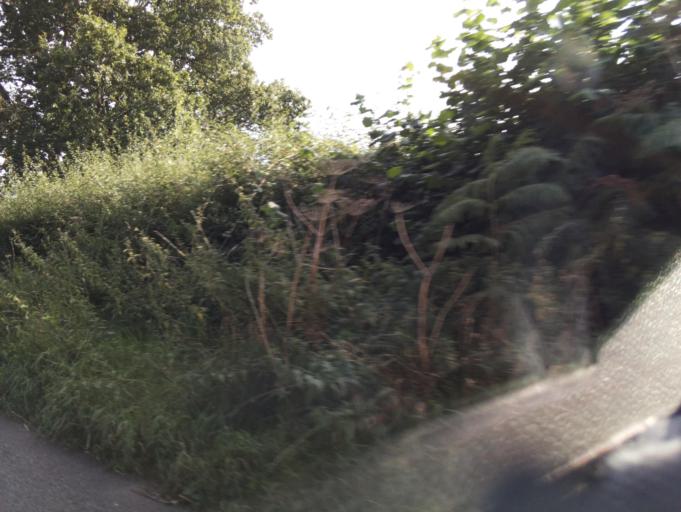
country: GB
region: England
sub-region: Devon
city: Tiverton
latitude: 50.8531
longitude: -3.5071
